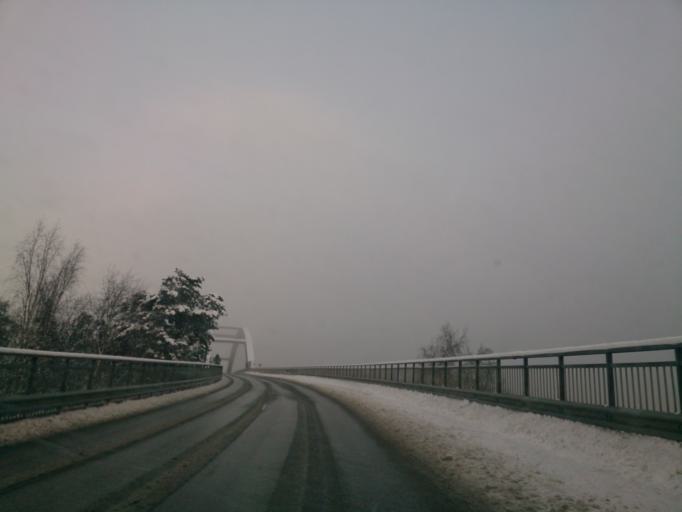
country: SE
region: Stockholm
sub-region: Varmdo Kommun
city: Holo
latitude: 59.2921
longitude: 18.6675
